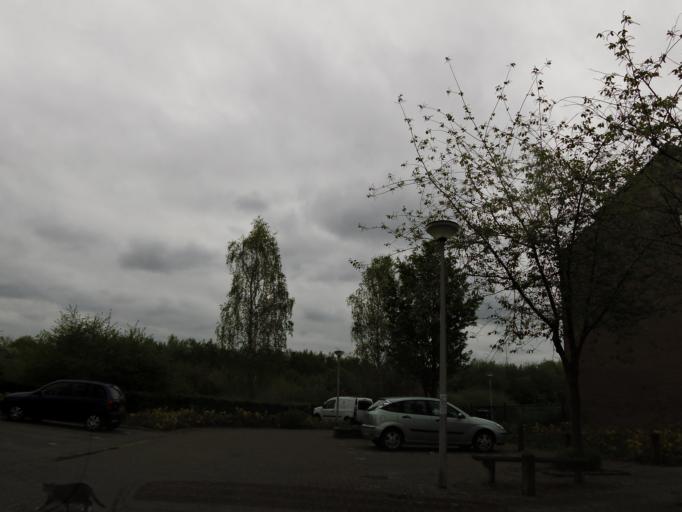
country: NL
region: Limburg
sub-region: Gemeente Kerkrade
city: Kerkrade
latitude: 50.8771
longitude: 6.0734
